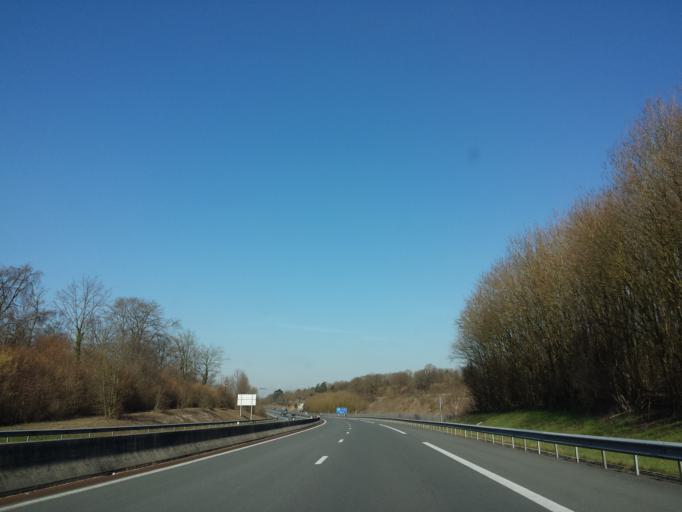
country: FR
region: Picardie
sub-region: Departement de la Somme
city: Saleux
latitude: 49.8371
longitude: 2.2528
